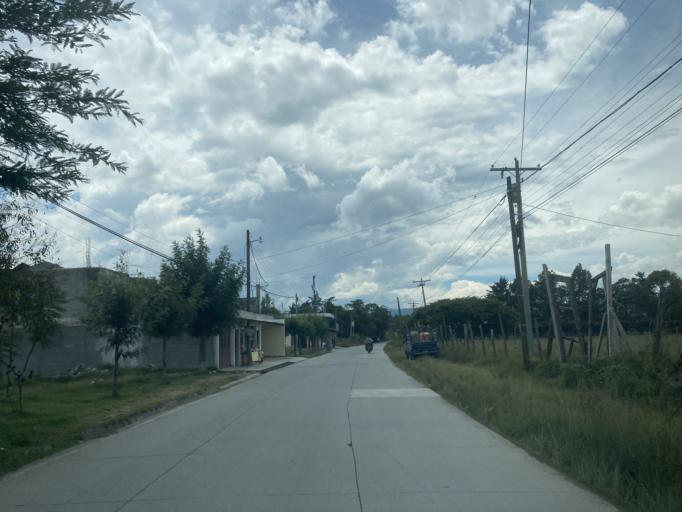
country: GT
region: Huehuetenango
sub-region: Municipio de Huehuetenango
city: Huehuetenango
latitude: 15.3306
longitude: -91.4894
